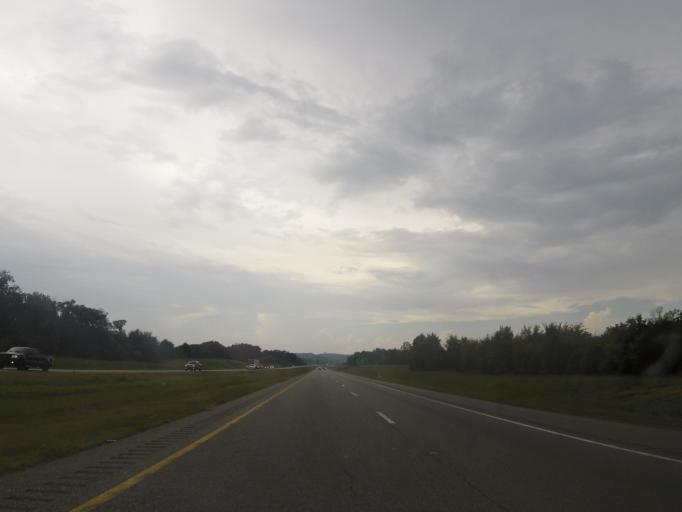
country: US
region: Tennessee
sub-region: Rutherford County
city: Smyrna
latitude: 35.8613
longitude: -86.5621
